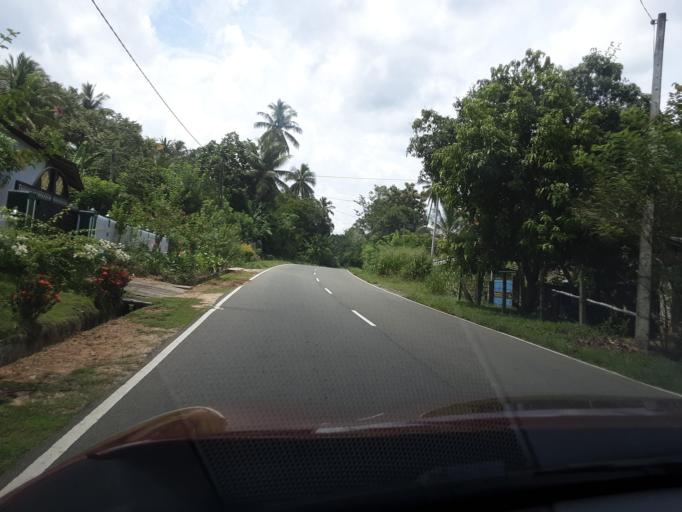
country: LK
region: Uva
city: Monaragala
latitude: 6.8912
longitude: 81.2938
